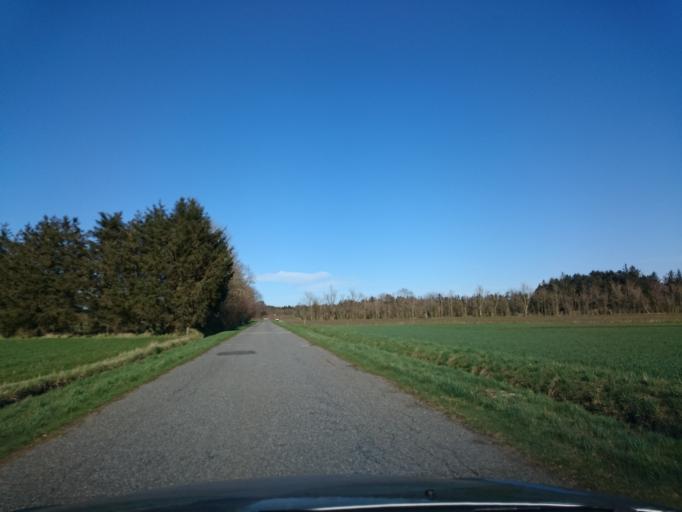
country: DK
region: North Denmark
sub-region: Hjorring Kommune
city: Hirtshals
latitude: 57.5633
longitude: 10.0774
